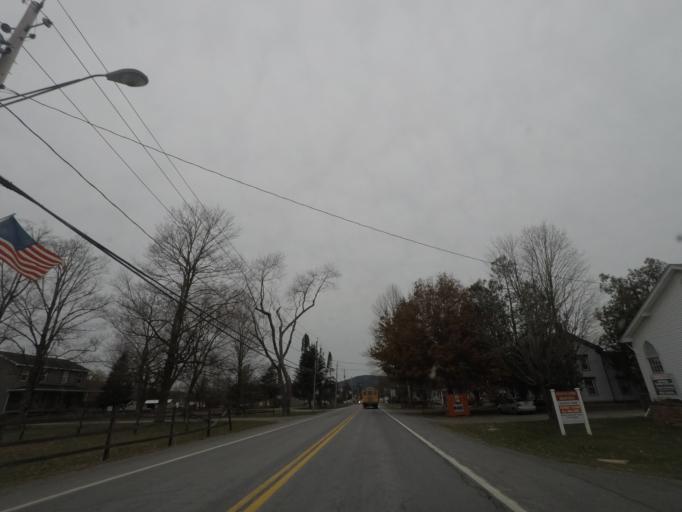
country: US
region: Massachusetts
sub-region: Berkshire County
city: Lanesborough
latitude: 42.5483
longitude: -73.3716
